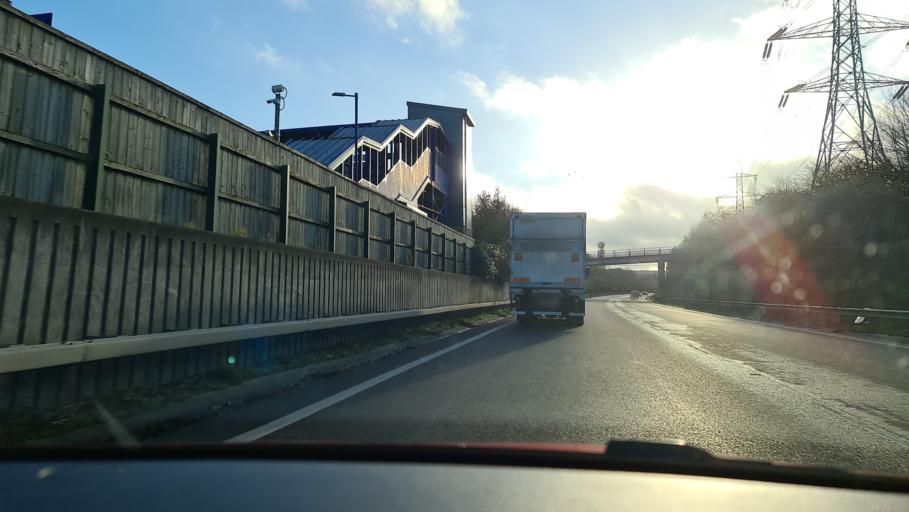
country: GB
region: England
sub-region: Buckinghamshire
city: Wendover
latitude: 51.7616
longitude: -0.7480
